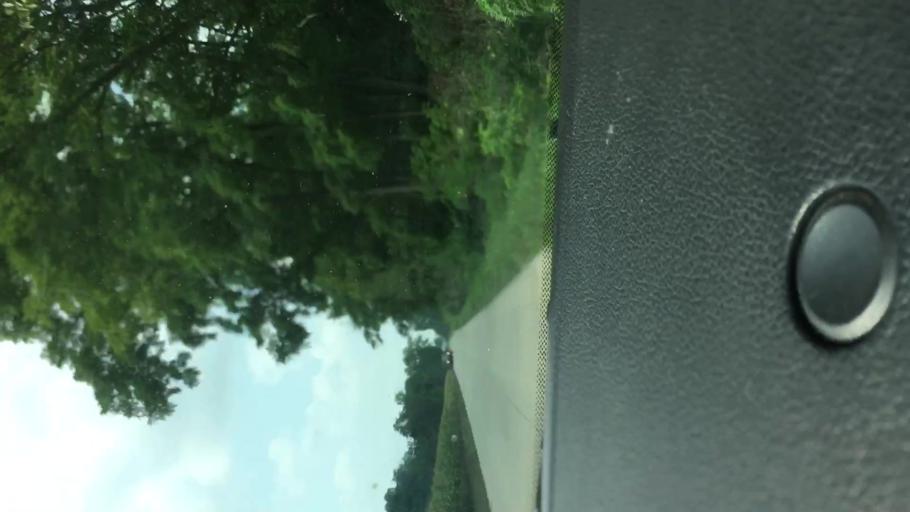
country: US
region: Ohio
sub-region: Mercer County
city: Fort Recovery
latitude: 40.3823
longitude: -84.8748
